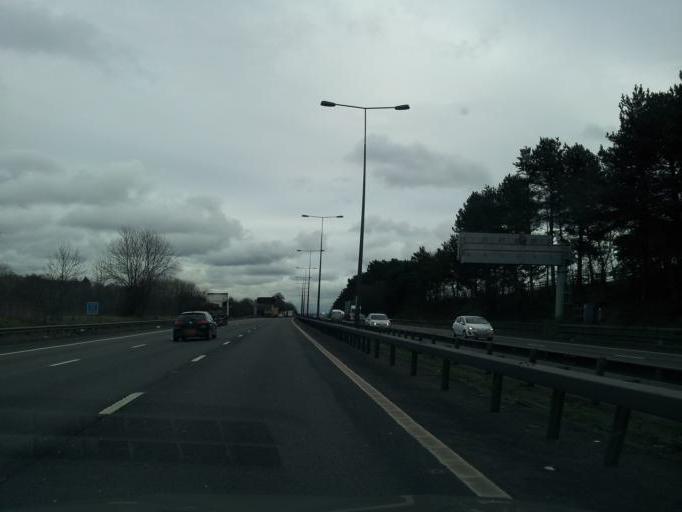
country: GB
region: England
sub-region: Staffordshire
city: Newcastle under Lyme
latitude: 52.9922
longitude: -2.2760
